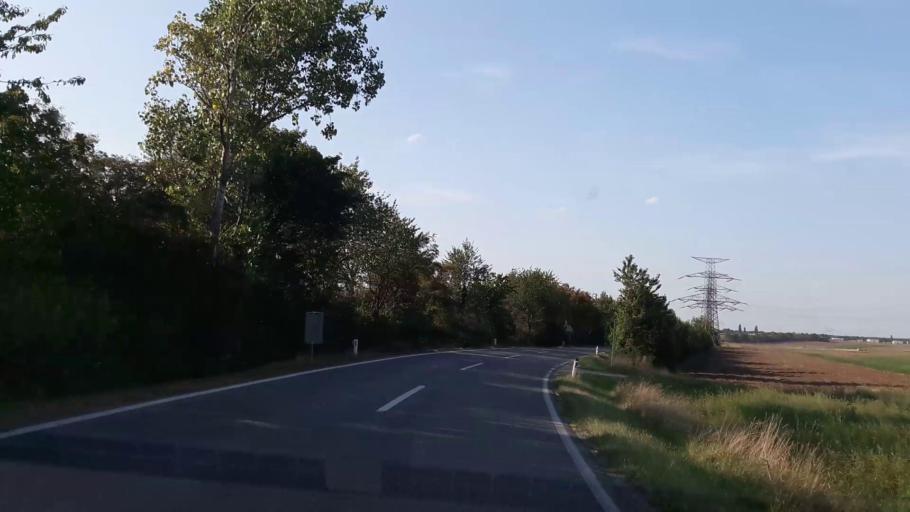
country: AT
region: Lower Austria
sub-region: Politischer Bezirk Ganserndorf
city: Mannsdorf an der Donau
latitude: 48.0929
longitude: 16.6680
